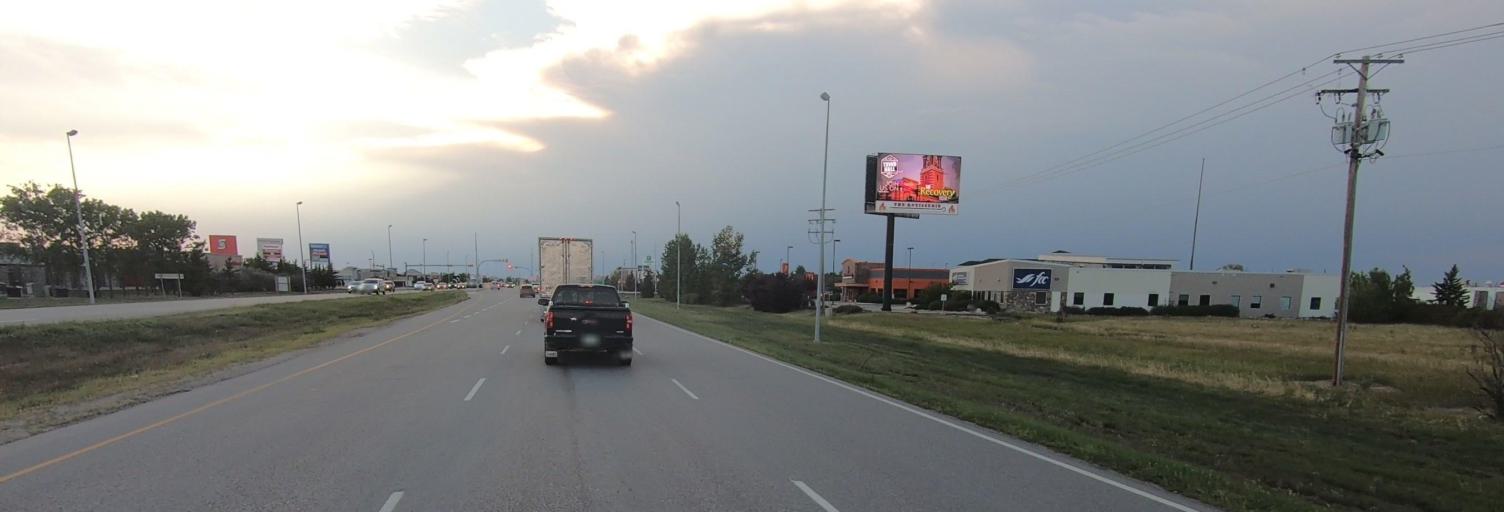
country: CA
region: Saskatchewan
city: Regina
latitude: 50.4477
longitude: -104.5294
